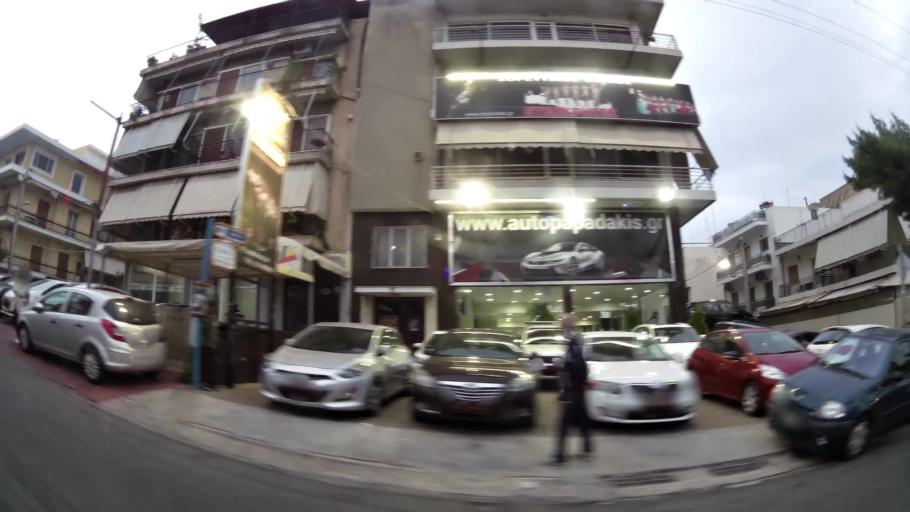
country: GR
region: Attica
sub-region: Nomos Piraios
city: Keratsini
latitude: 37.9652
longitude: 23.6148
